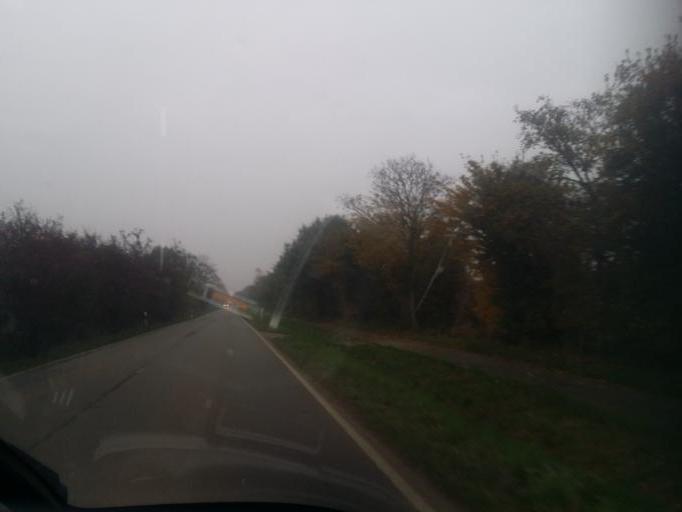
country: DE
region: Schleswig-Holstein
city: Satrup
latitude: 54.6951
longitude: 9.5829
